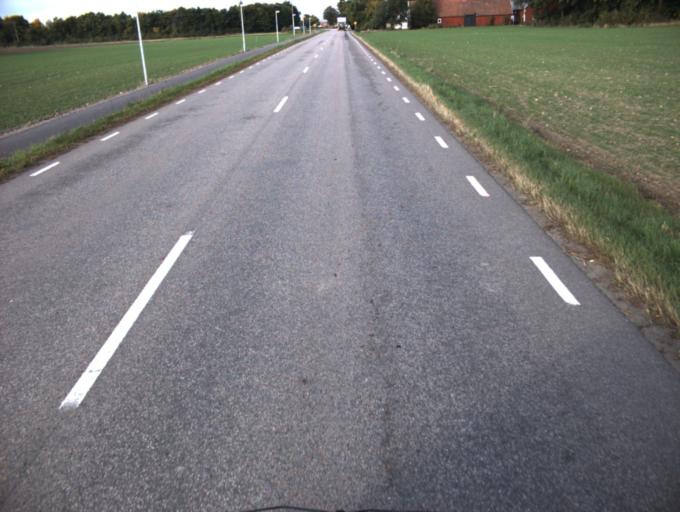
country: SE
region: Skane
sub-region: Helsingborg
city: Odakra
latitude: 56.1089
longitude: 12.7646
